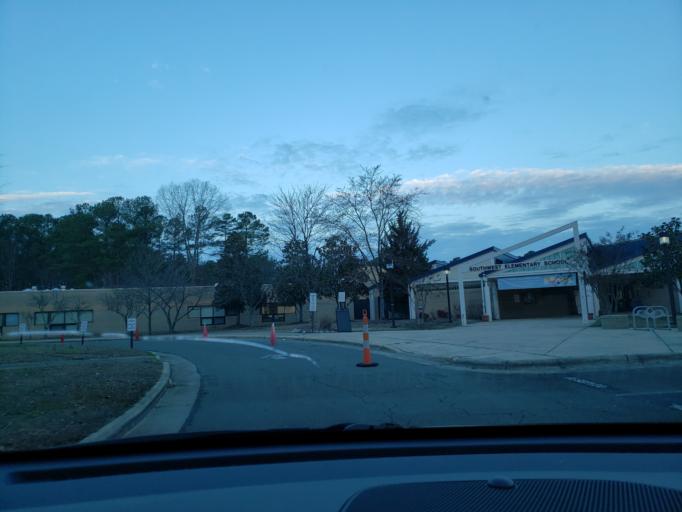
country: US
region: North Carolina
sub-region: Durham County
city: Durham
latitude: 35.9285
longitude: -78.9232
